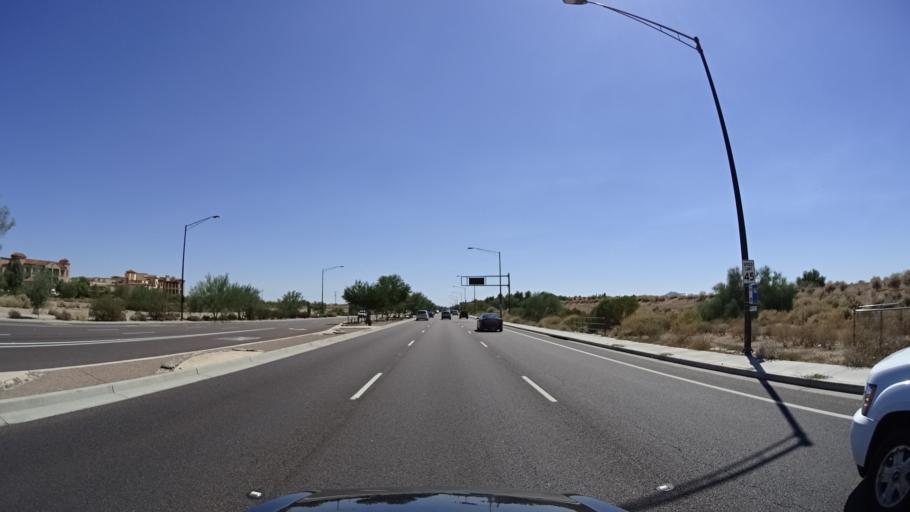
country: US
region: Arizona
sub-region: Maricopa County
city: Paradise Valley
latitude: 33.6463
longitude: -111.9255
